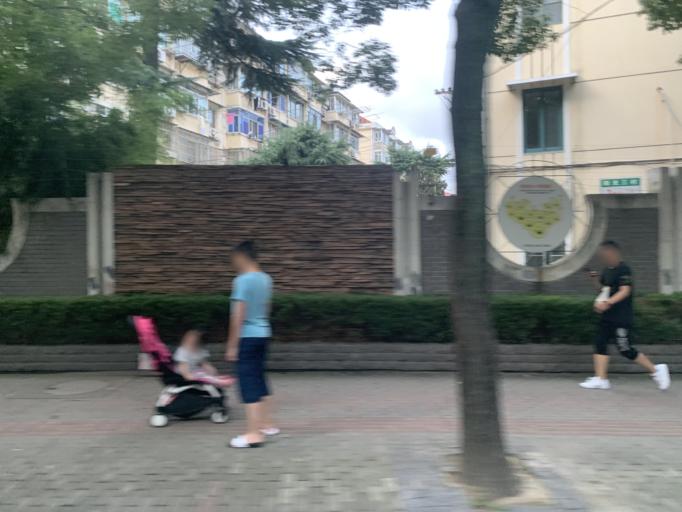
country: CN
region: Shanghai Shi
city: Pudong
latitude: 31.2485
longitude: 121.5482
